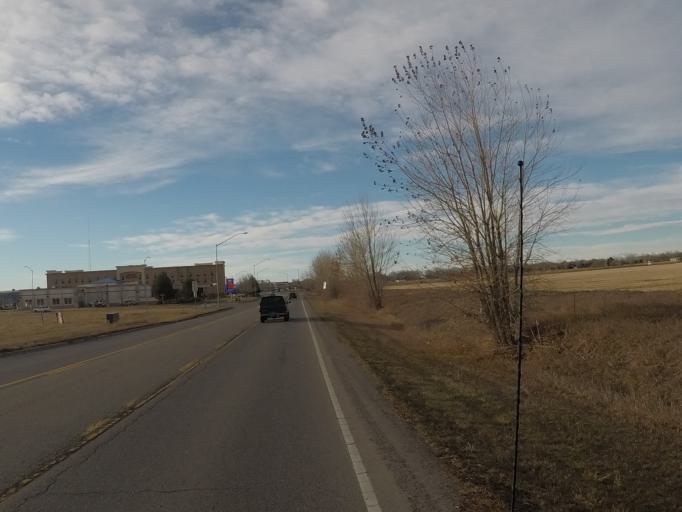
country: US
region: Montana
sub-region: Yellowstone County
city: Billings
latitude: 45.7386
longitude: -108.6071
